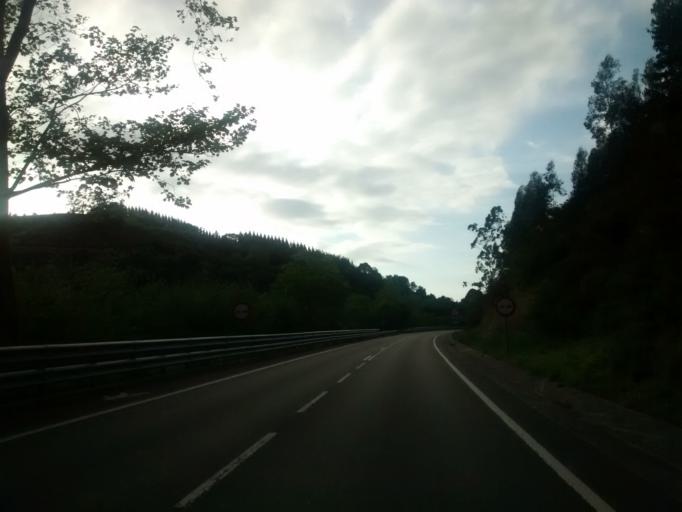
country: ES
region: Cantabria
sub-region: Provincia de Cantabria
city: San Vicente de la Barquera
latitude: 43.2926
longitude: -4.4543
